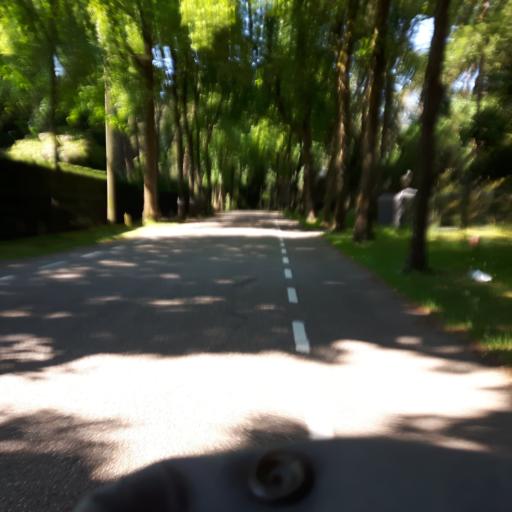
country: NL
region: Utrecht
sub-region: Gemeente Zeist
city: Zeist
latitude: 52.1269
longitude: 5.2416
